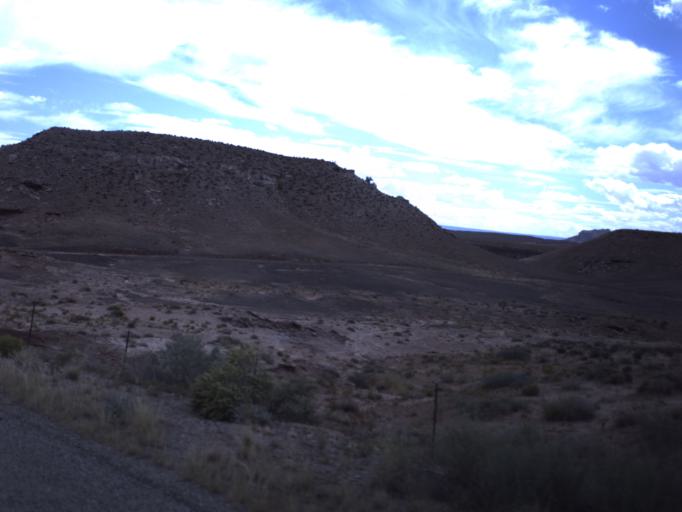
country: US
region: Utah
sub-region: San Juan County
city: Blanding
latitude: 37.2835
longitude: -109.3843
